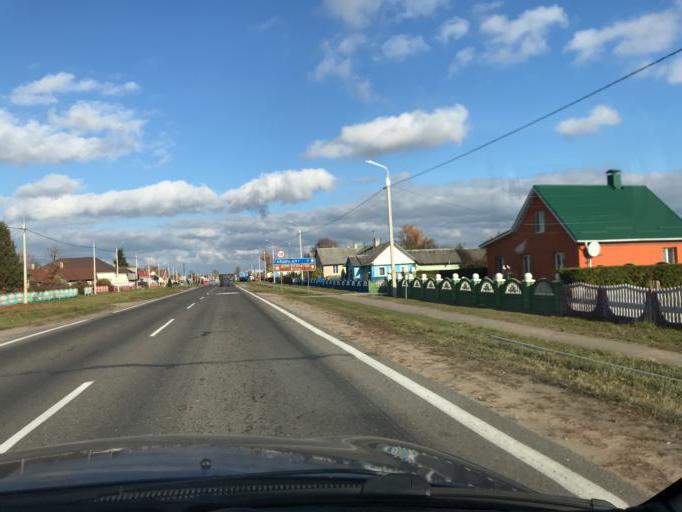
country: LT
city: Salcininkai
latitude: 54.2477
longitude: 25.3559
